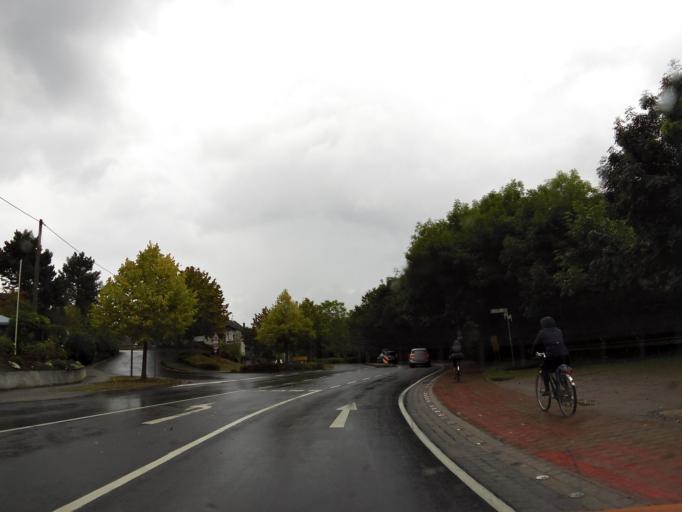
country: DE
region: Rheinland-Pfalz
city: Brieden
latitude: 50.1690
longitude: 7.2690
